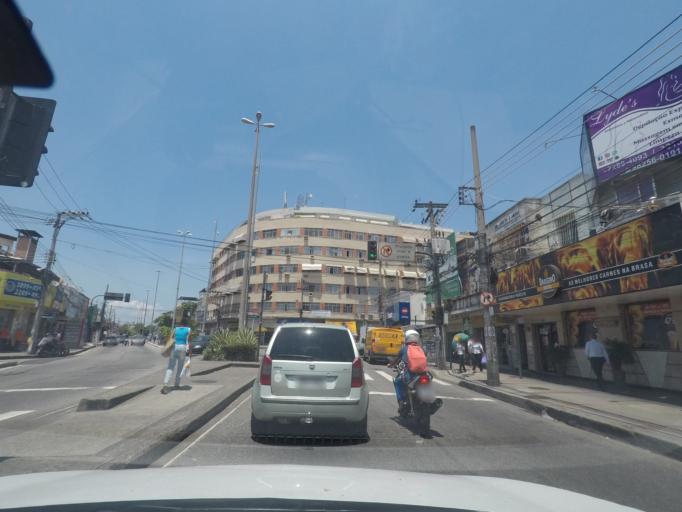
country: BR
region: Rio de Janeiro
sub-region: Rio De Janeiro
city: Rio de Janeiro
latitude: -22.8852
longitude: -43.2986
